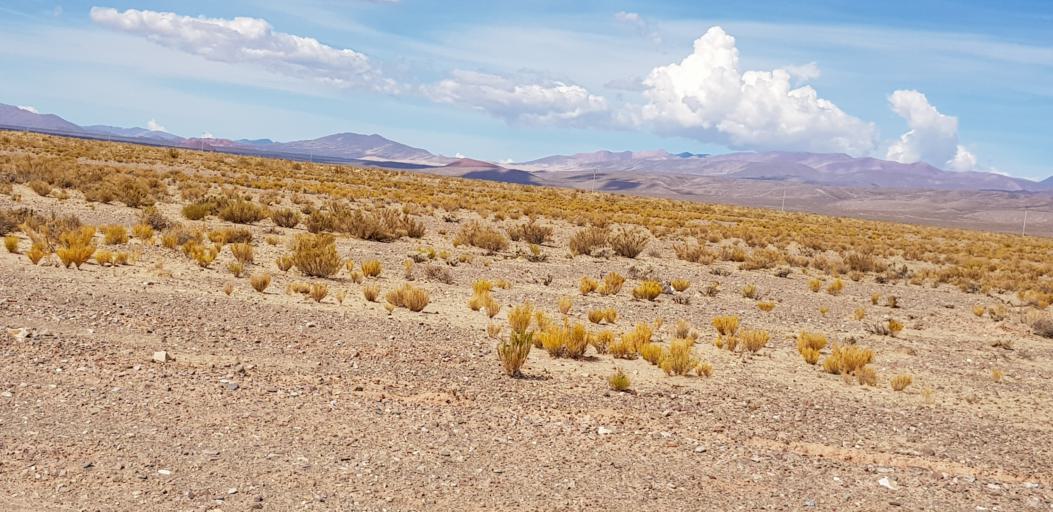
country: AR
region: Jujuy
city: Maimara
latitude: -23.6386
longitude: -65.8431
